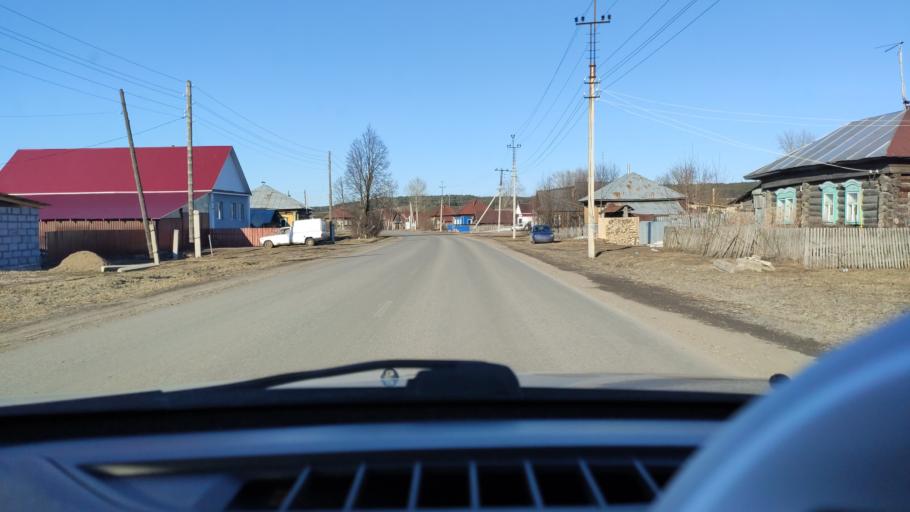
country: RU
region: Perm
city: Suksun
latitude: 57.0326
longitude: 57.4152
